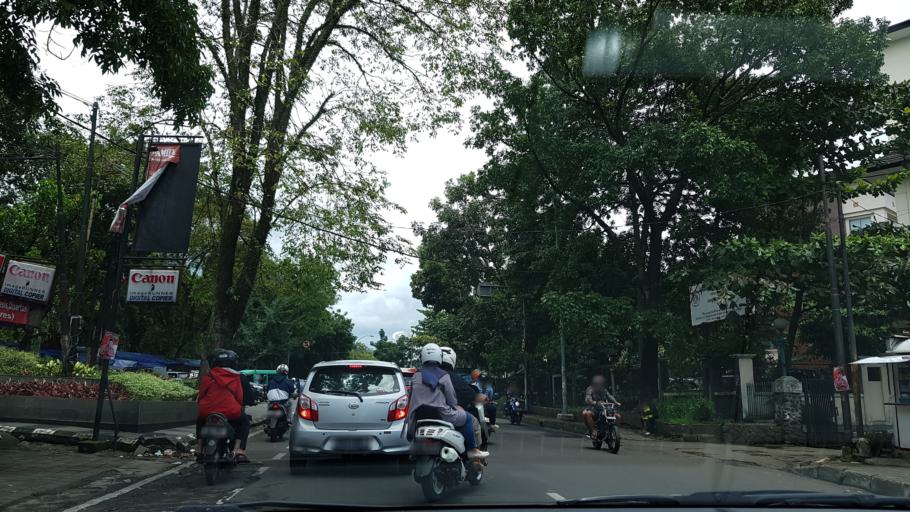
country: ID
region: West Java
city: Bandung
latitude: -6.8951
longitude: 107.6172
